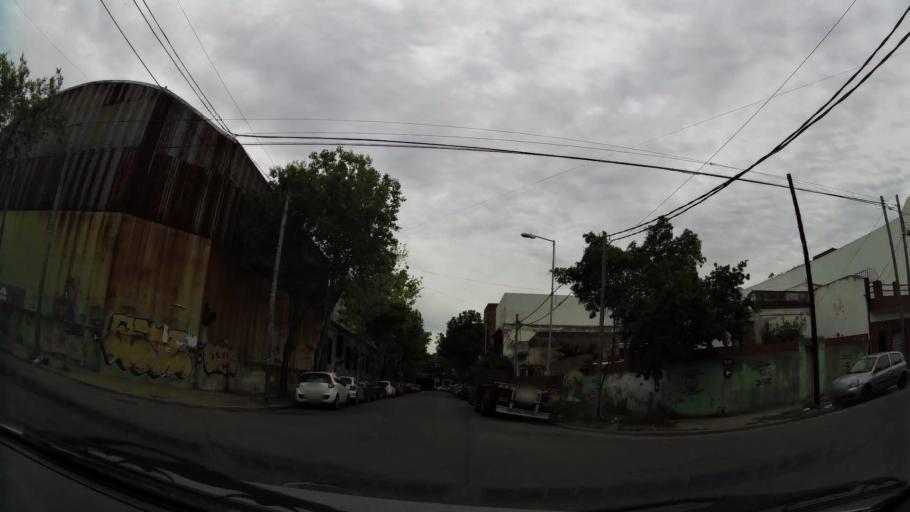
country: AR
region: Buenos Aires
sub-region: Partido de Avellaneda
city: Avellaneda
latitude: -34.6748
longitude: -58.3837
